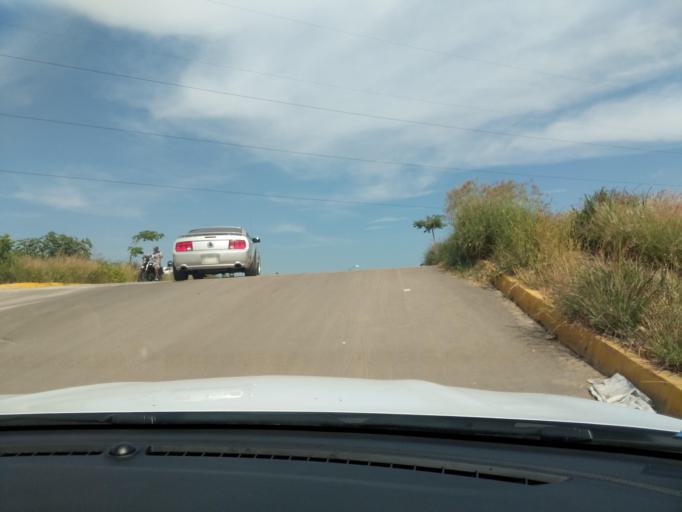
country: MX
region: Jalisco
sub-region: El Salto
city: El Muey
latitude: 20.5207
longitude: -103.2201
